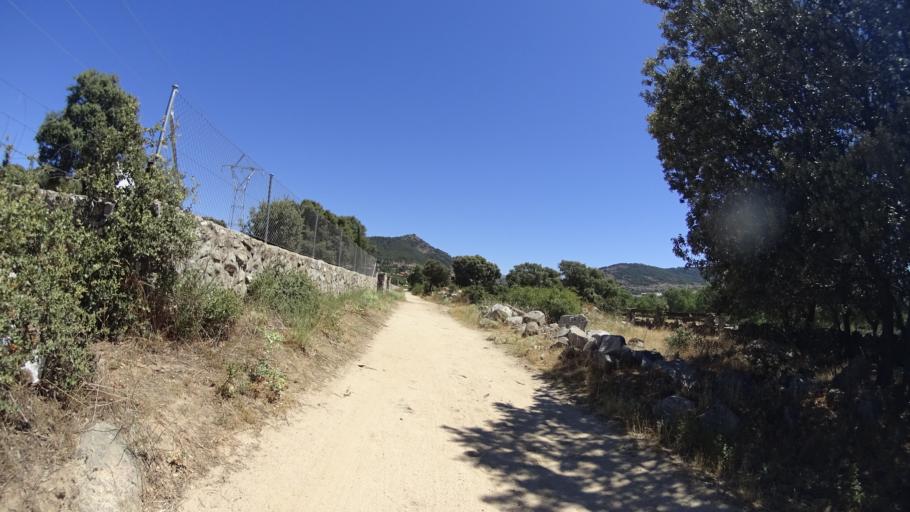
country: ES
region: Madrid
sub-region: Provincia de Madrid
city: Collado Mediano
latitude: 40.6827
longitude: -4.0376
